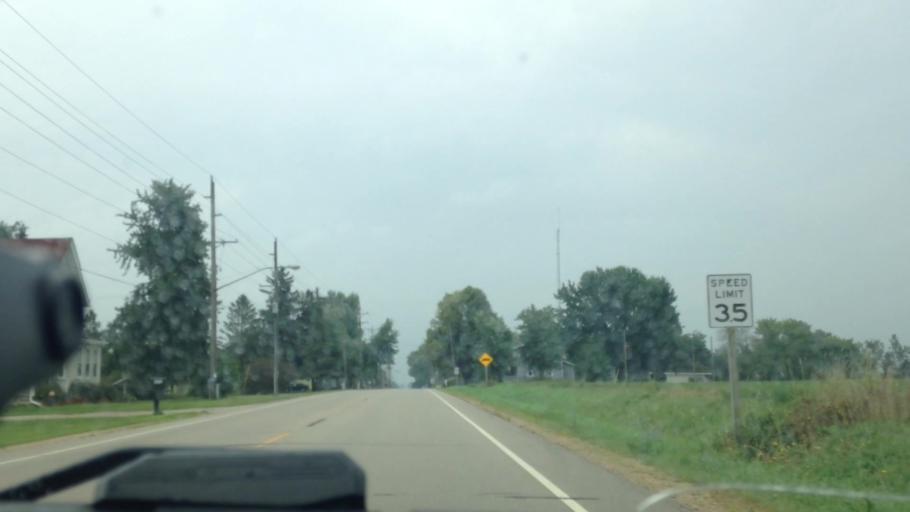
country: US
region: Wisconsin
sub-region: Washington County
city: Slinger
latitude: 43.3731
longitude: -88.3367
